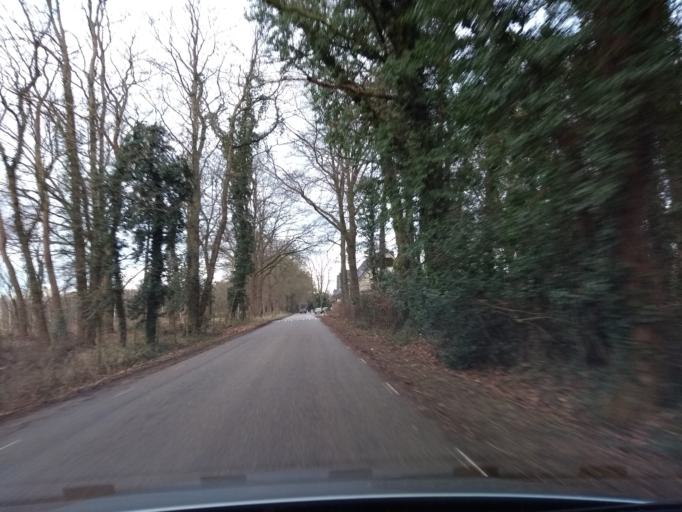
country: NL
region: Overijssel
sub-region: Gemeente Enschede
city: Enschede
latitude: 52.2475
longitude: 6.8851
